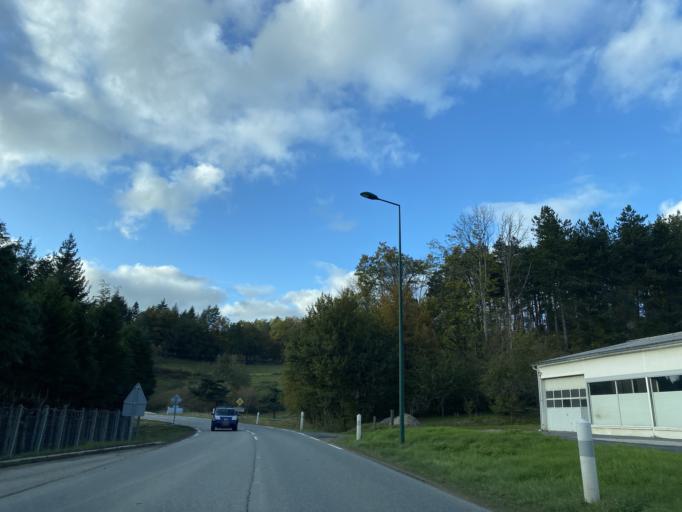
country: FR
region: Auvergne
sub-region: Departement du Puy-de-Dome
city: Job
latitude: 45.6479
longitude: 3.6989
